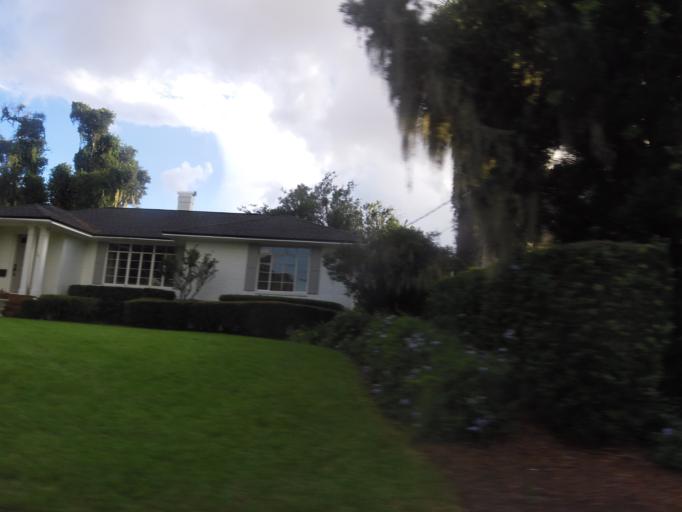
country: US
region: Florida
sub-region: Duval County
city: Jacksonville
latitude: 30.2885
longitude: -81.6574
